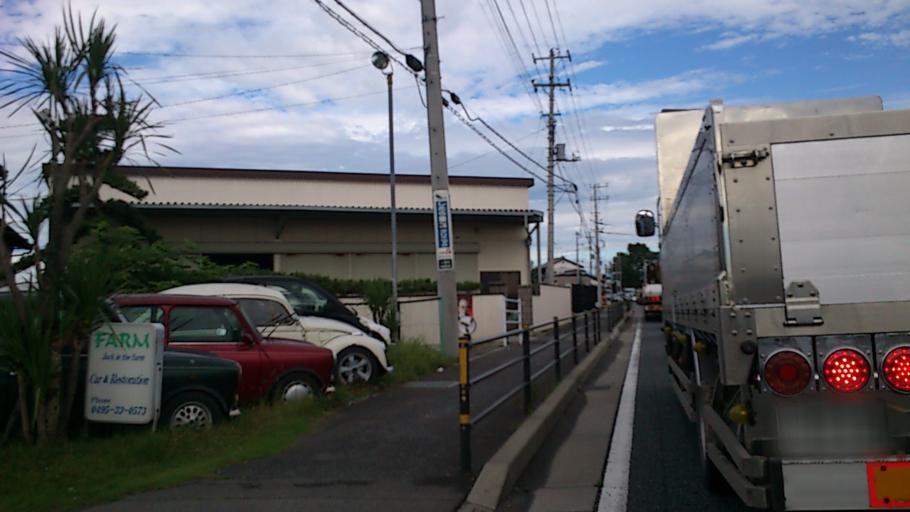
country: JP
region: Gunma
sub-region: Sawa-gun
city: Tamamura
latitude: 36.2653
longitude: 139.1280
